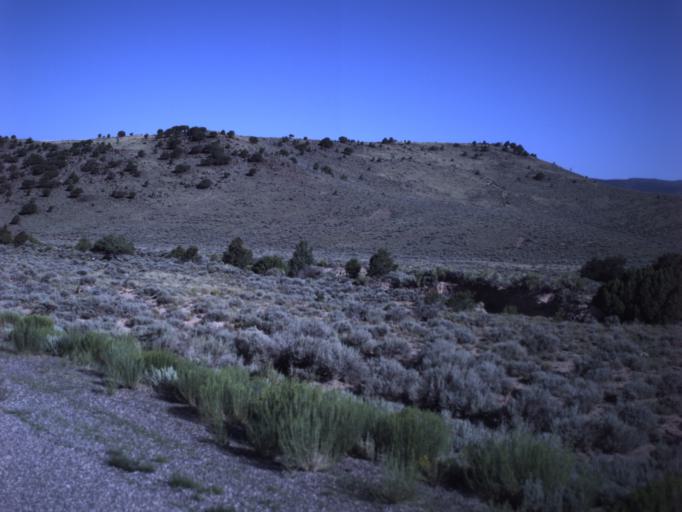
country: US
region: Utah
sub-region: Wayne County
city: Loa
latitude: 38.4793
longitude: -111.5623
